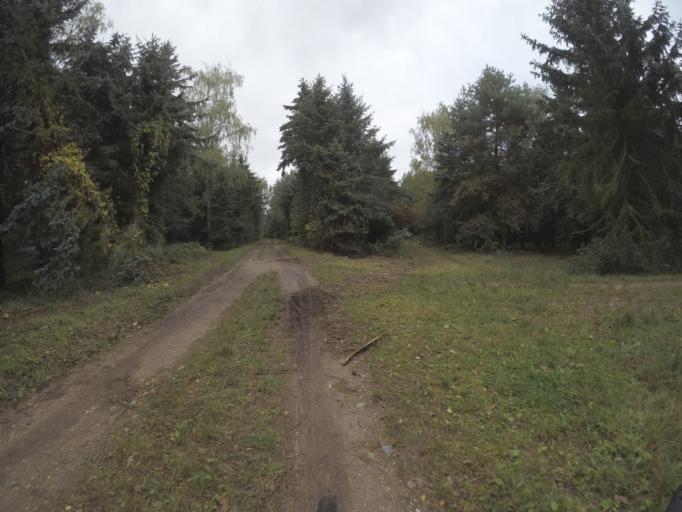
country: DE
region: Berlin
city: Buch
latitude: 52.6544
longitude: 13.4922
